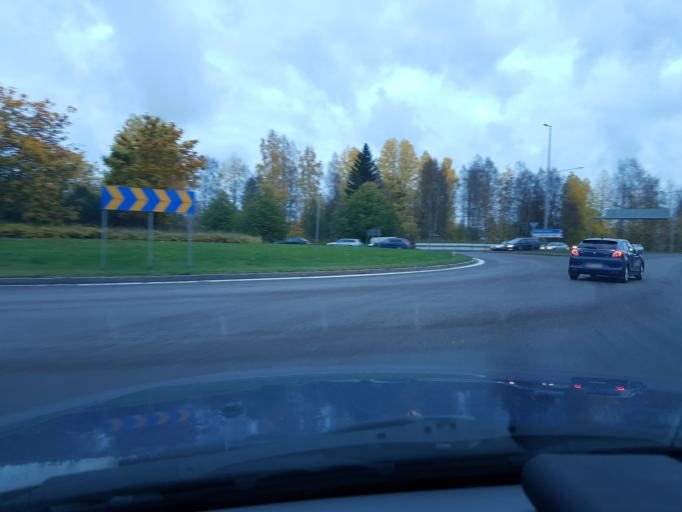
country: SE
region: Vaesterbotten
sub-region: Skelleftea Kommun
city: Skelleftea
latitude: 64.7432
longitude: 20.9599
